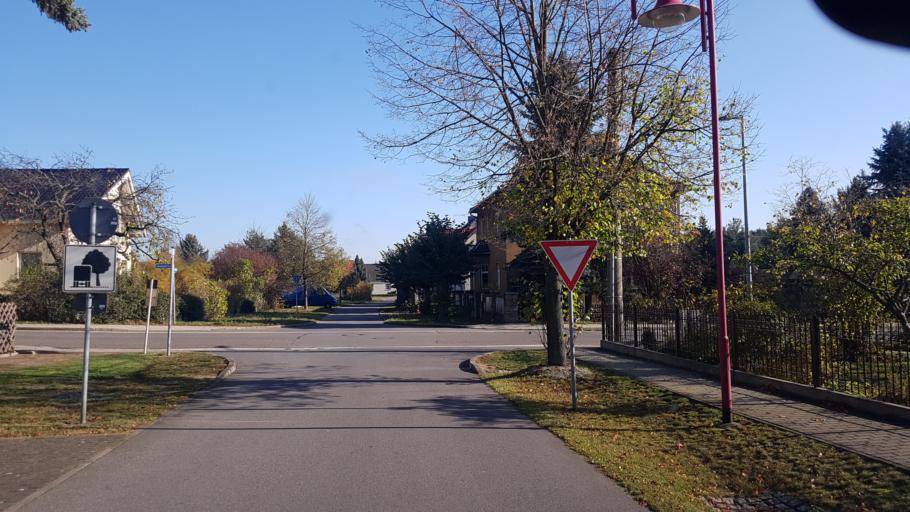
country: DE
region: Brandenburg
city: Hohenleipisch
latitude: 51.4964
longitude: 13.5655
